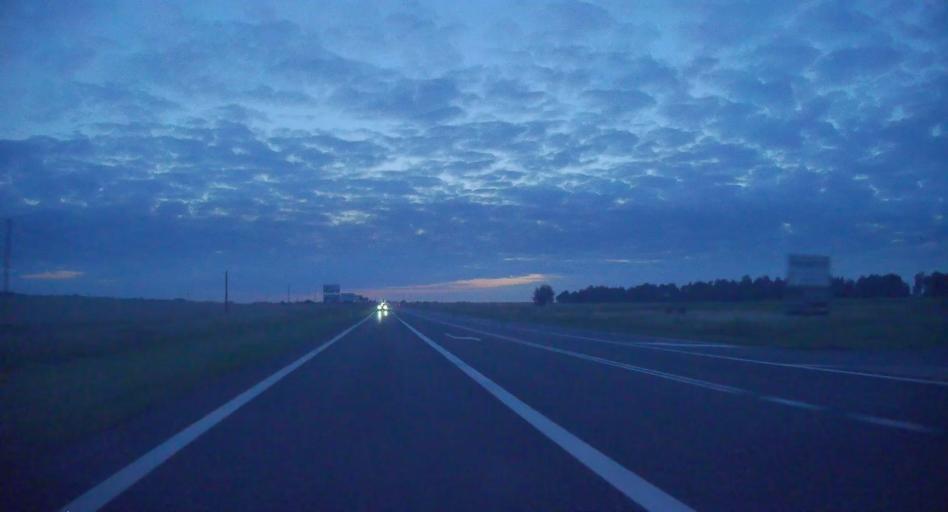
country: PL
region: Silesian Voivodeship
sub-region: Powiat klobucki
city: Klobuck
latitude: 50.8871
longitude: 18.9764
